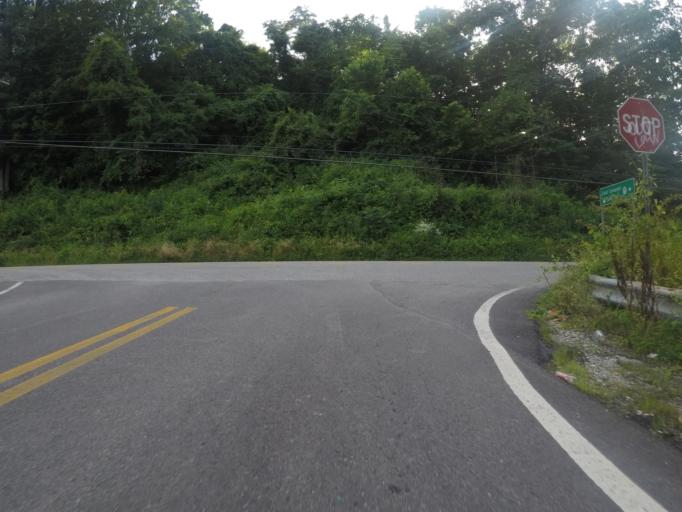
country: US
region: West Virginia
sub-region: Cabell County
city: Pea Ridge
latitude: 38.4040
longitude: -82.3650
